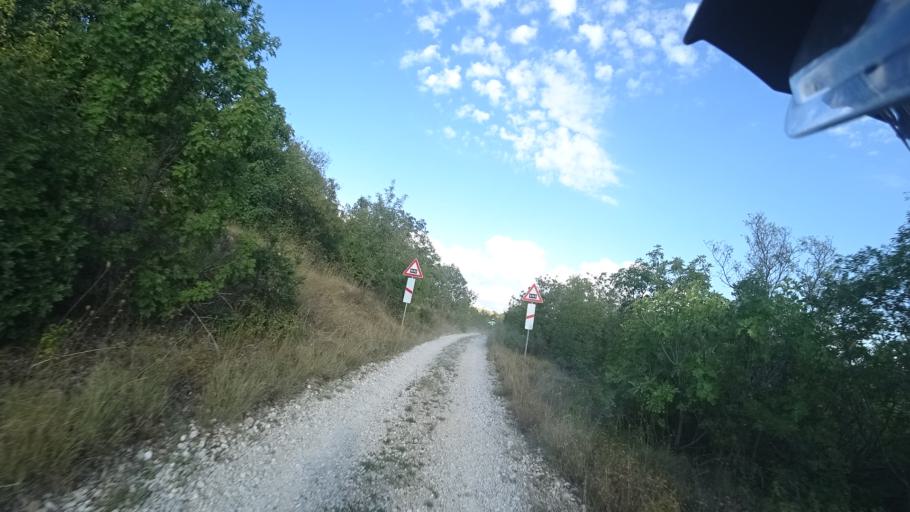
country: HR
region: Sibensko-Kniniska
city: Knin
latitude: 44.1374
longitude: 16.1130
